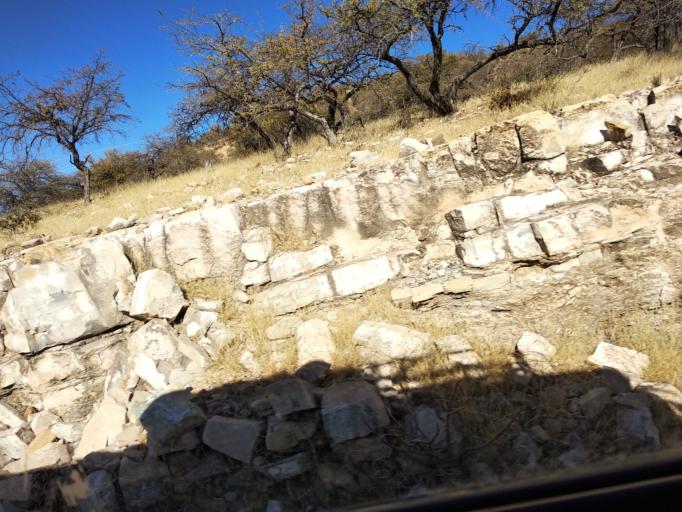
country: BO
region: Cochabamba
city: Mizque
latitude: -18.0841
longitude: -65.7516
